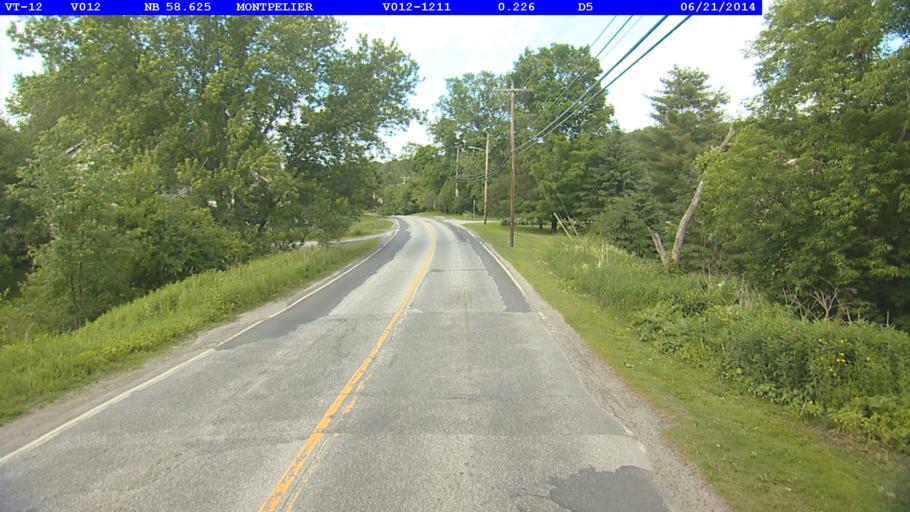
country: US
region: Vermont
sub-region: Washington County
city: Montpelier
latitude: 44.2481
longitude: -72.5844
